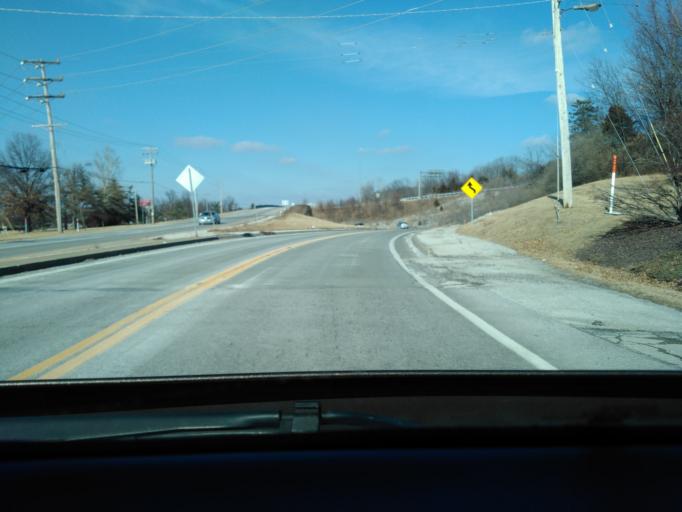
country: US
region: Missouri
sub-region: Saint Louis County
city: Manchester
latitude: 38.6264
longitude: -90.5156
